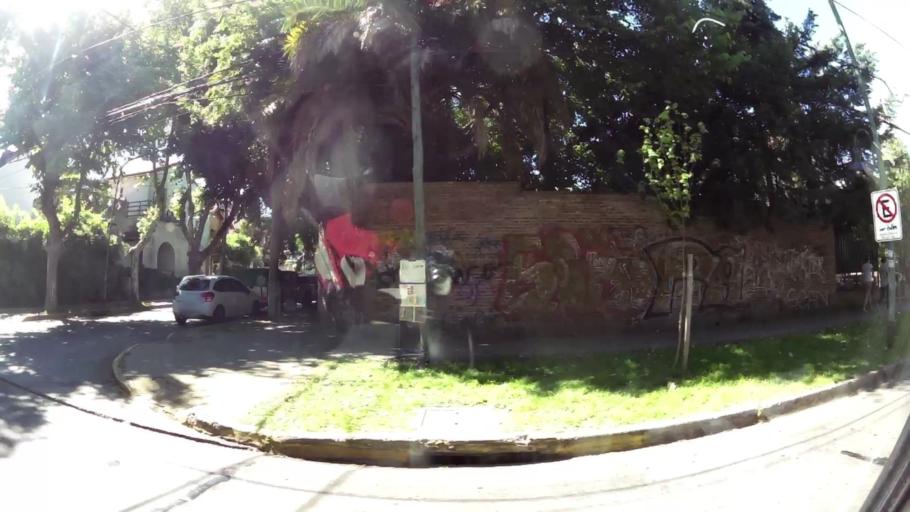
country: AR
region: Buenos Aires
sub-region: Partido de Vicente Lopez
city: Olivos
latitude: -34.5202
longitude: -58.4837
